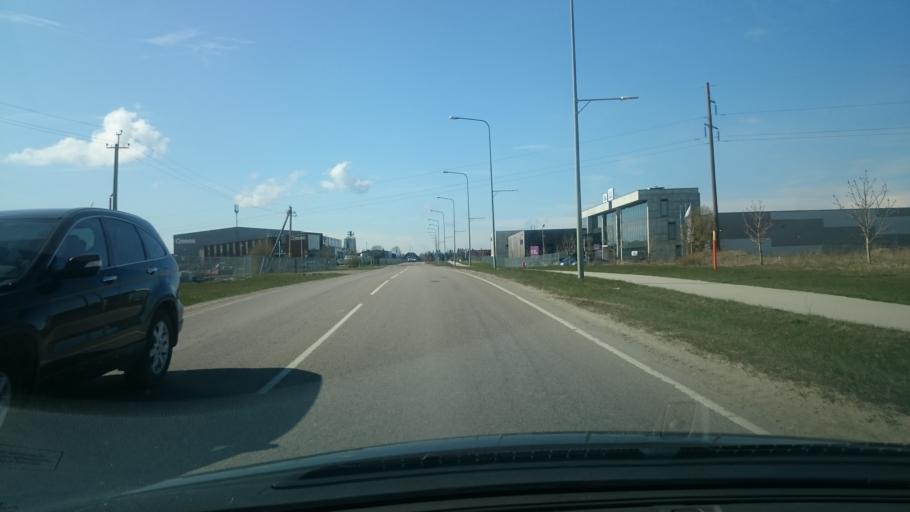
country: EE
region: Harju
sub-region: Rae vald
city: Jueri
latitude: 59.3611
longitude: 24.8817
